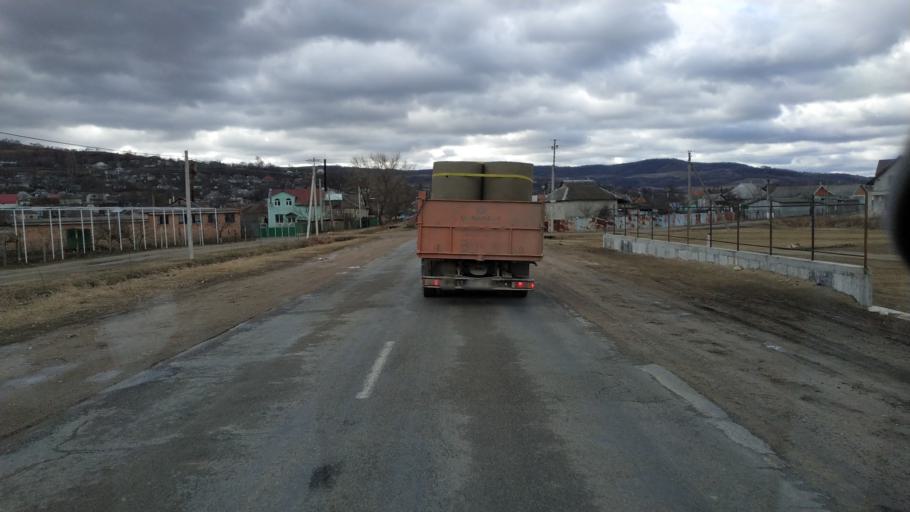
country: MD
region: Stinga Nistrului
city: Bucovat
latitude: 47.1614
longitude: 28.4344
